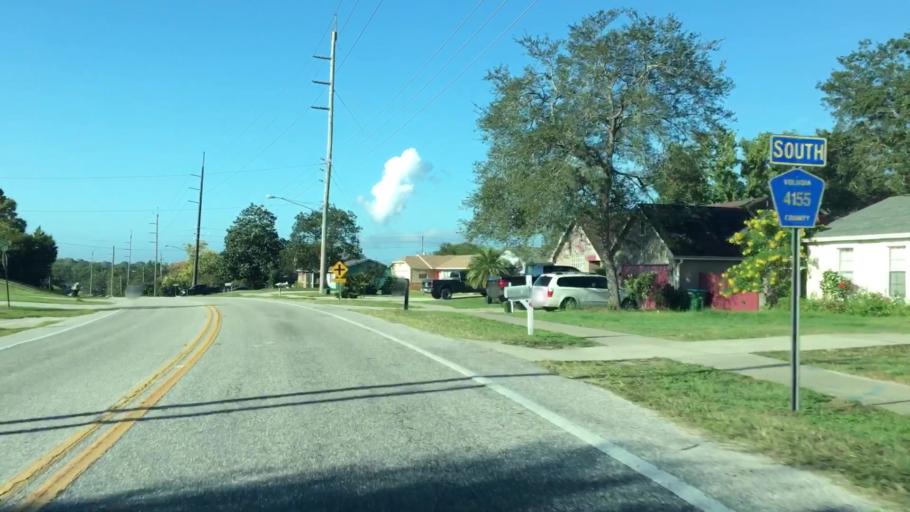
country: US
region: Florida
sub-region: Volusia County
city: Deltona
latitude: 28.8778
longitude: -81.2497
